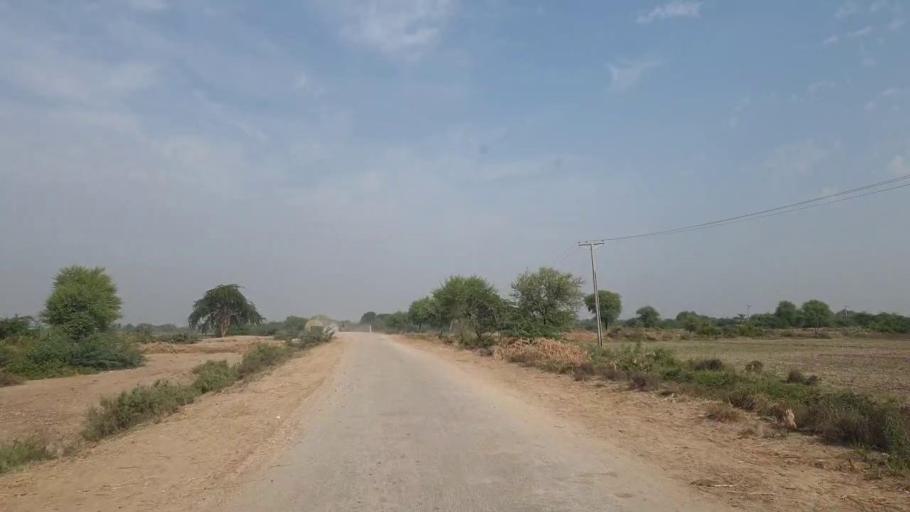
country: PK
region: Sindh
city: Tando Bago
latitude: 24.9281
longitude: 68.9879
